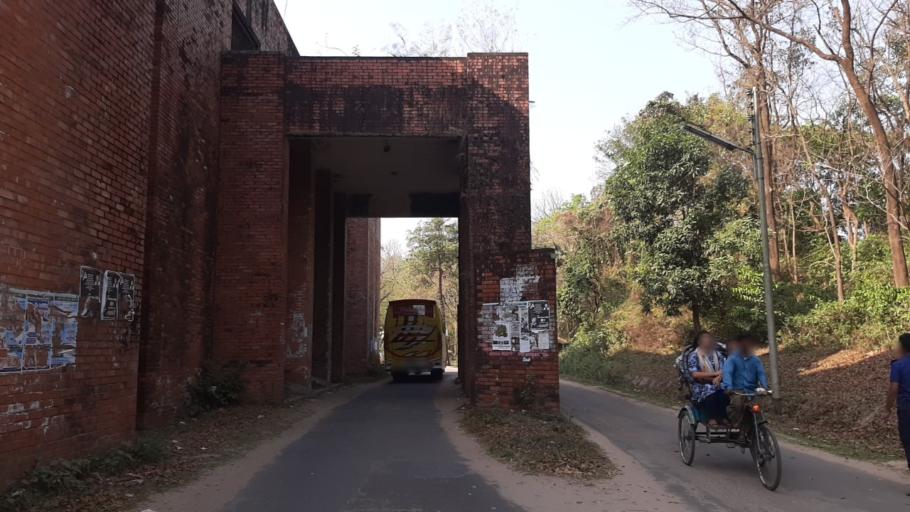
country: BD
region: Chittagong
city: Raojan
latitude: 22.4756
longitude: 91.7915
